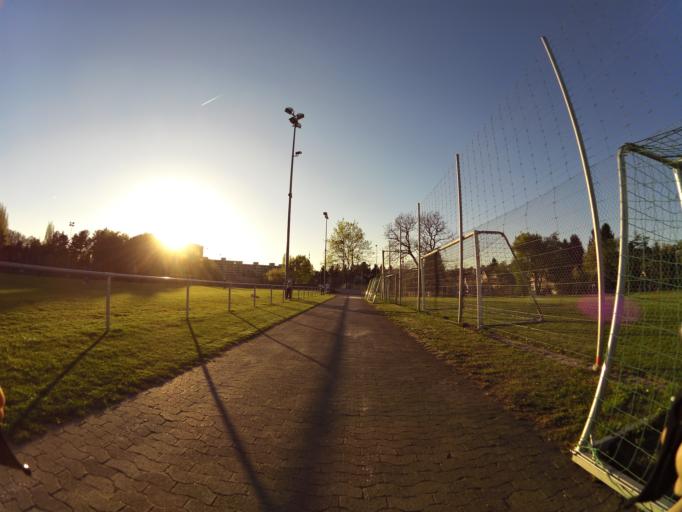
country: CH
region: Zurich
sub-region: Bezirk Zuerich
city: Zuerich (Kreis 10) / Hoengg
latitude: 47.3952
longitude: 8.4967
